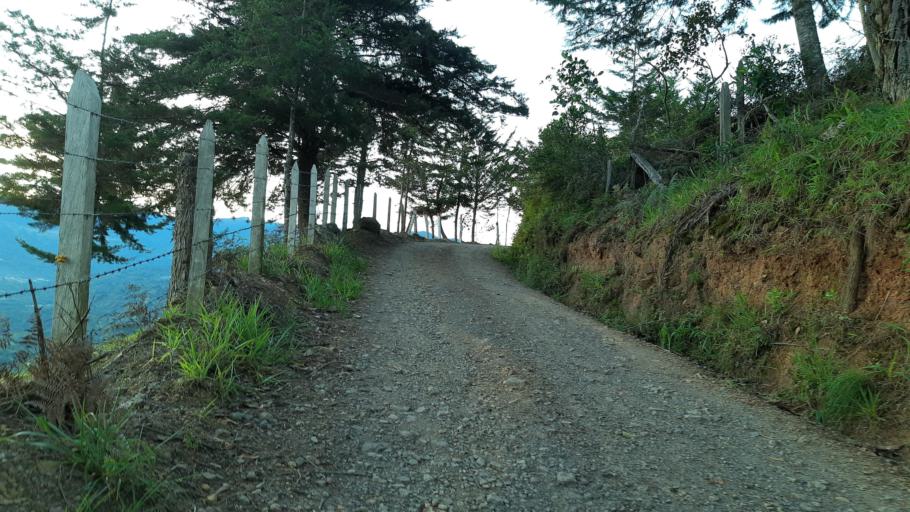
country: CO
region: Boyaca
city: Garagoa
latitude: 5.0569
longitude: -73.3778
